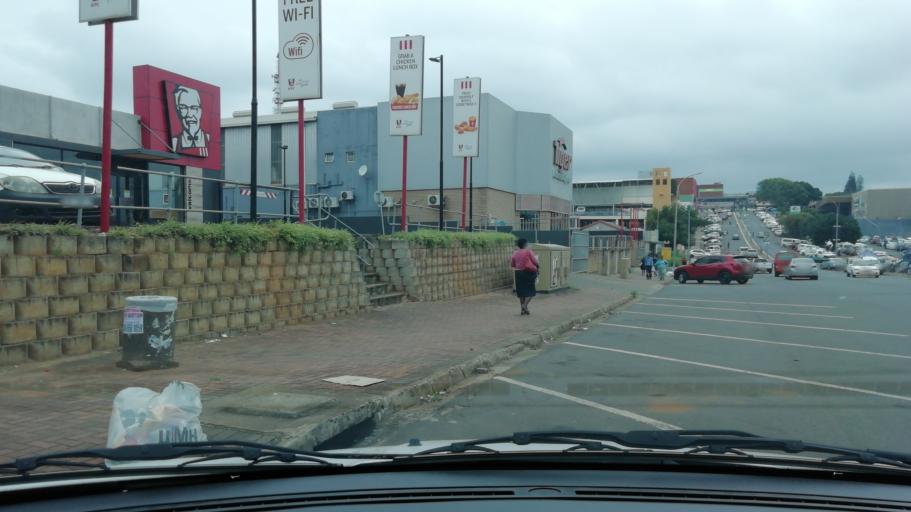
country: ZA
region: KwaZulu-Natal
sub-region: uThungulu District Municipality
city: Empangeni
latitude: -28.7410
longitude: 31.8922
